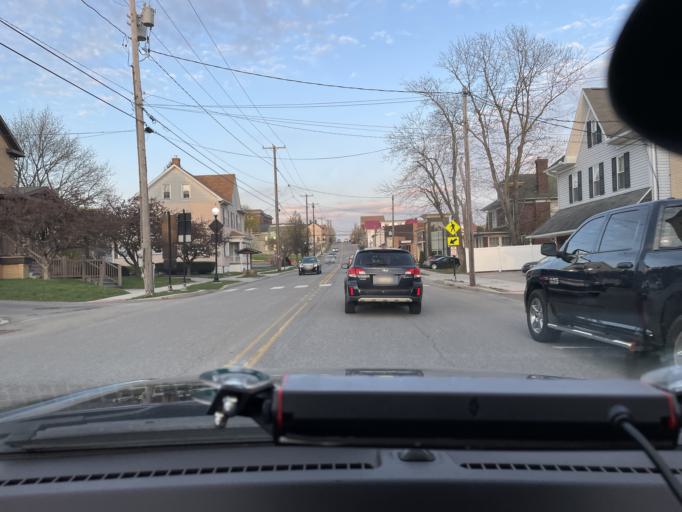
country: US
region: Pennsylvania
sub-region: Cambria County
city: Ebensburg
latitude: 40.4852
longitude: -78.7306
